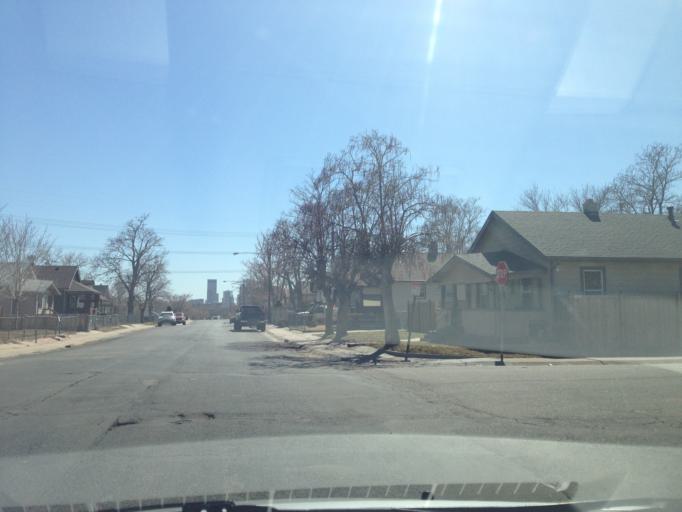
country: US
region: Colorado
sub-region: Adams County
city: Twin Lakes
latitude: 39.7857
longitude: -104.9859
